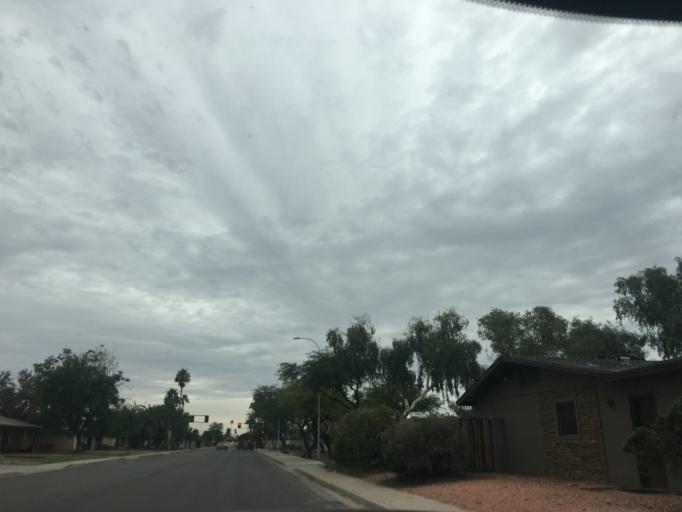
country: US
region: Arizona
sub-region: Maricopa County
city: Tempe
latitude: 33.3798
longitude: -111.9007
